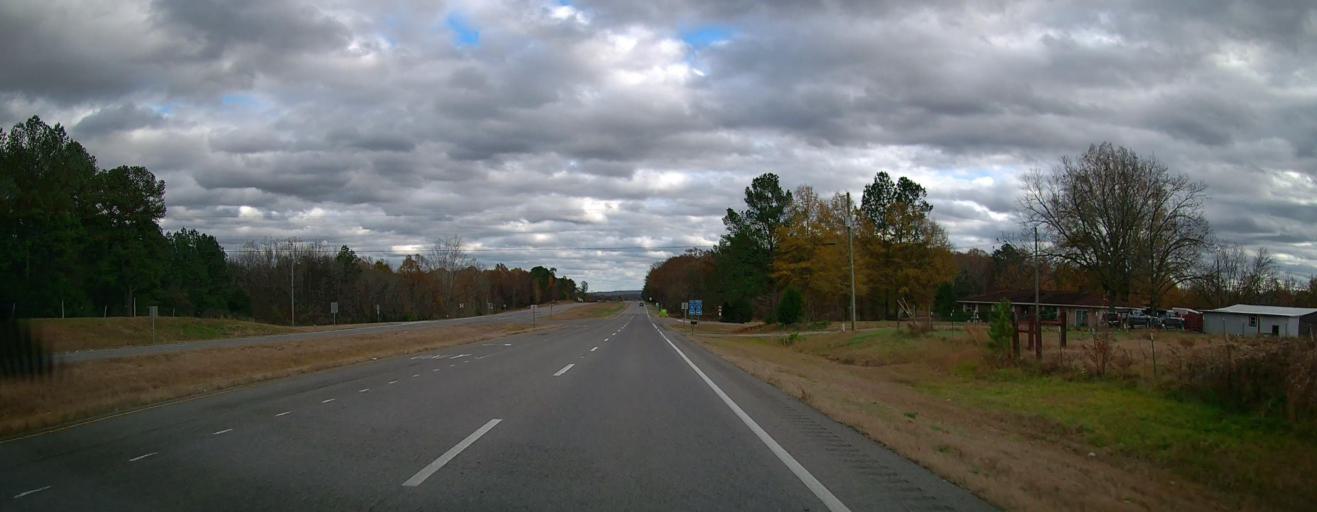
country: US
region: Alabama
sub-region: Morgan County
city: Danville
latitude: 34.3895
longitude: -87.1118
